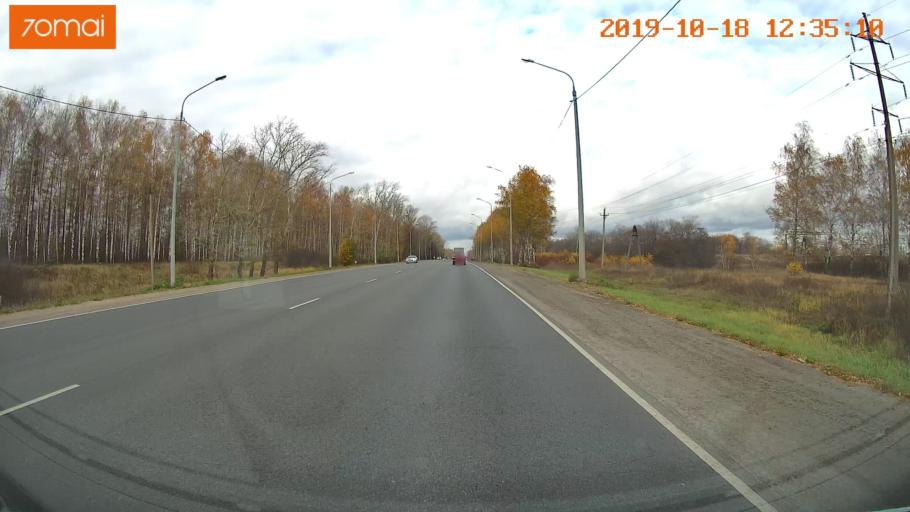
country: RU
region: Rjazan
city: Ryazan'
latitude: 54.6213
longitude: 39.6362
